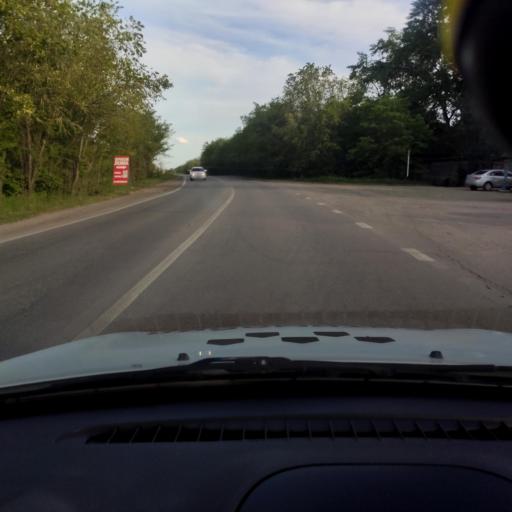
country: RU
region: Samara
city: Podstepki
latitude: 53.5979
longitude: 49.0412
